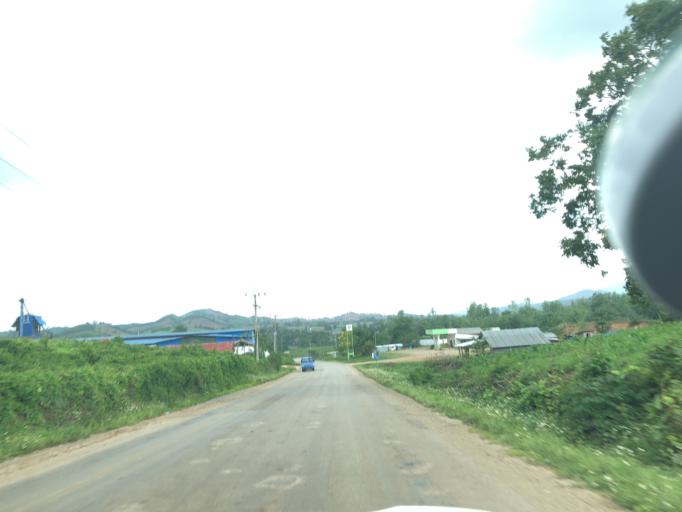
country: TH
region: Uttaradit
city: Ban Khok
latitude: 18.1192
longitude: 101.3728
